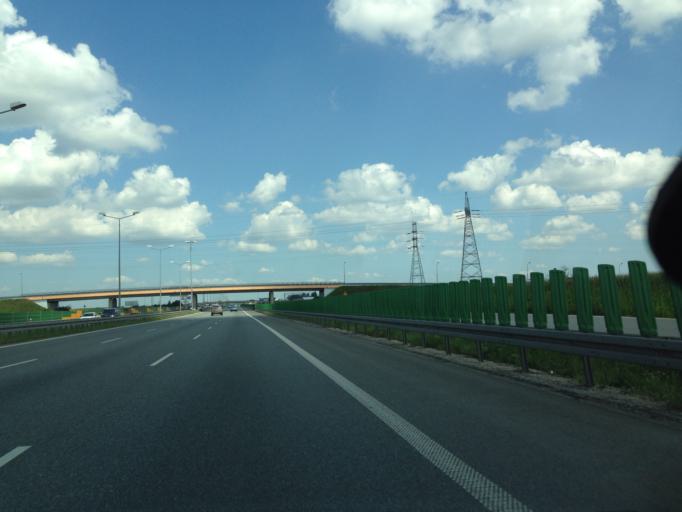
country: PL
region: Masovian Voivodeship
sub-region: Warszawa
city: Ursus
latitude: 52.2218
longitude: 20.8703
